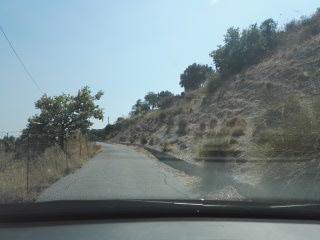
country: IT
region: Calabria
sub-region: Provincia di Reggio Calabria
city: Stilo
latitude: 38.4517
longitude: 16.4612
